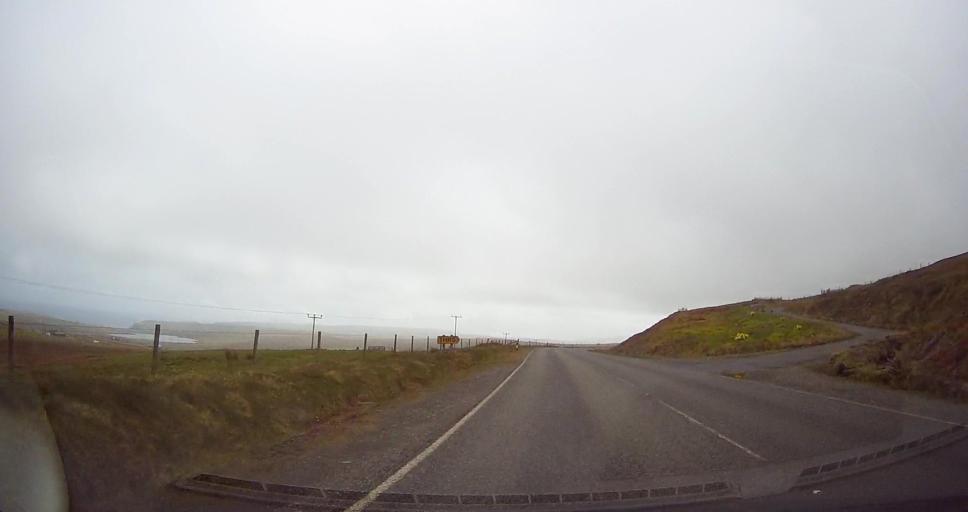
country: GB
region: Scotland
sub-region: Shetland Islands
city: Sandwick
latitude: 59.9574
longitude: -1.2865
